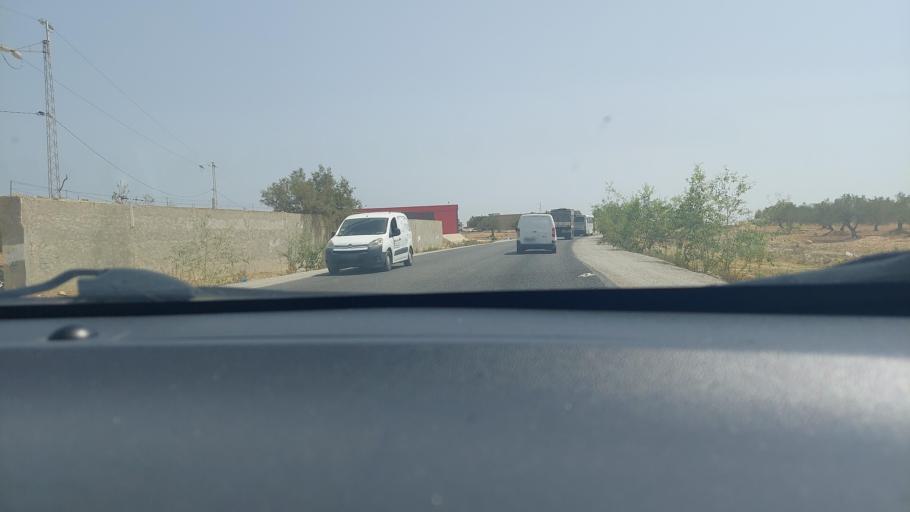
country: TN
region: Al Munastir
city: Qasr Hallal
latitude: 35.6376
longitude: 10.8675
